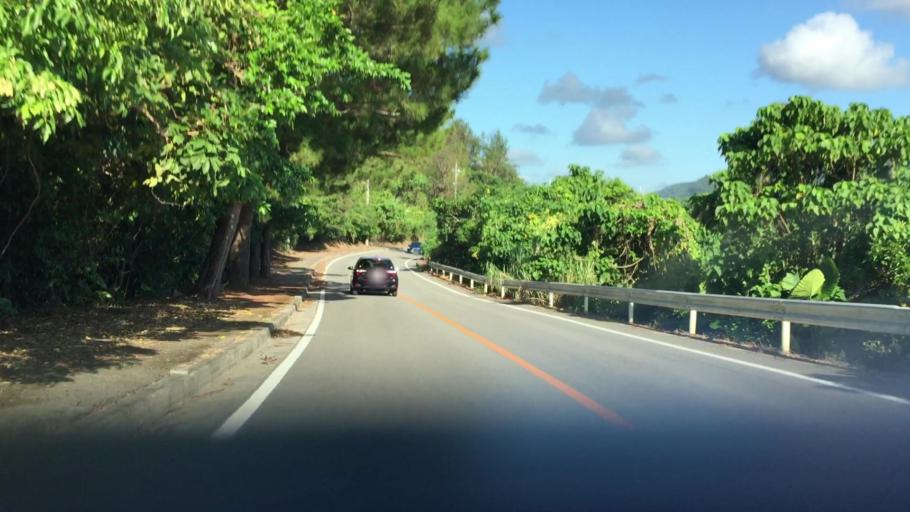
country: JP
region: Okinawa
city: Ishigaki
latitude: 24.4037
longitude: 124.1478
